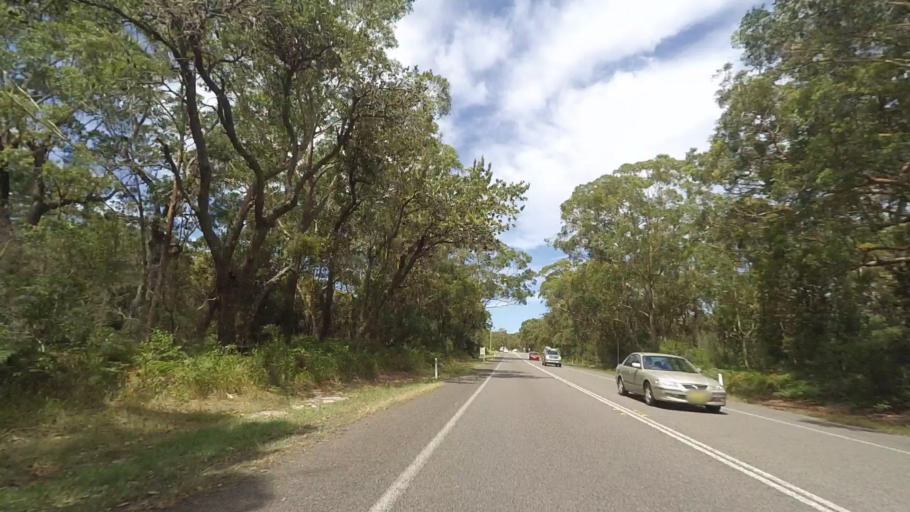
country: AU
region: New South Wales
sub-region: Port Stephens Shire
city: Medowie
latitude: -32.7930
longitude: 151.9494
